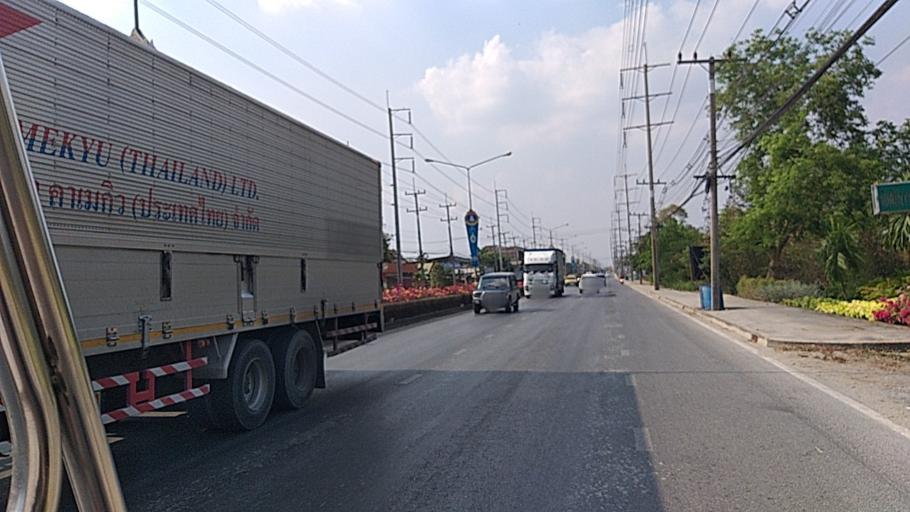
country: TH
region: Pathum Thani
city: Sam Khok
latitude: 14.0554
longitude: 100.5244
